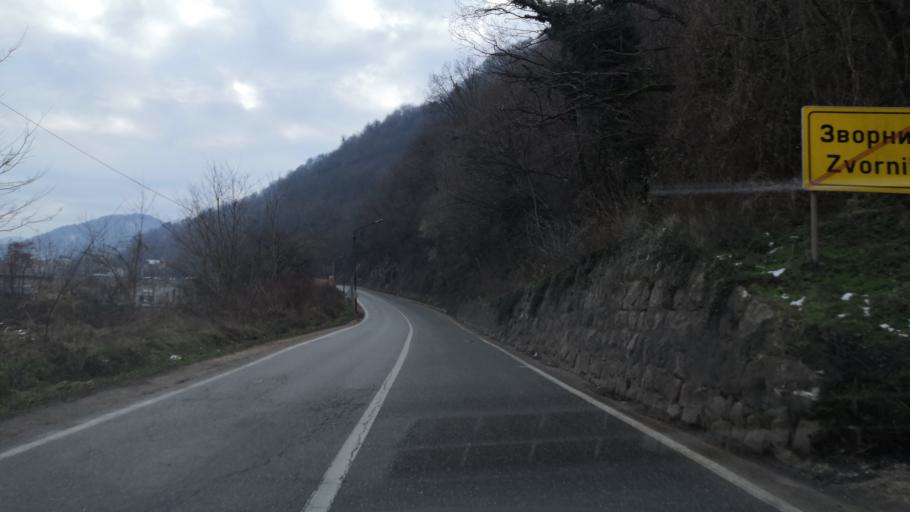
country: RS
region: Central Serbia
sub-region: Macvanski Okrug
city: Mali Zvornik
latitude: 44.3687
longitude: 19.1029
